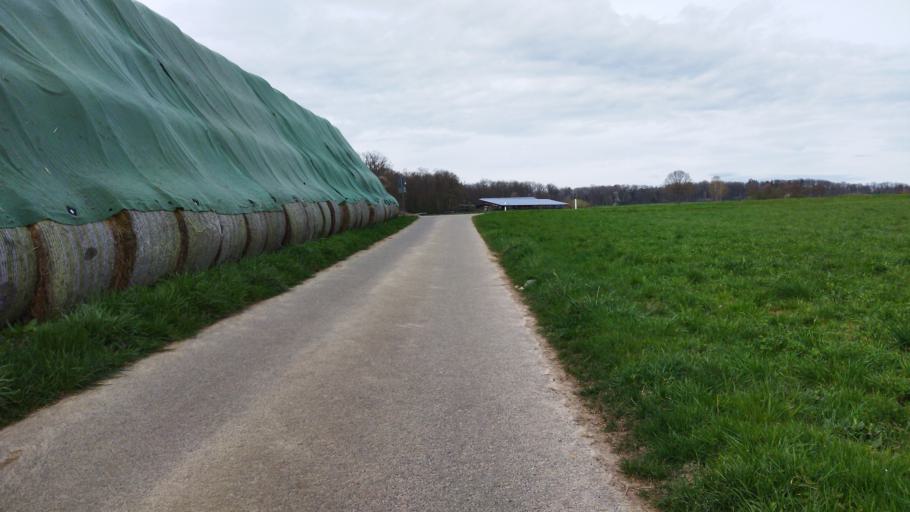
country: DE
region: Baden-Wuerttemberg
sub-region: Regierungsbezirk Stuttgart
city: Gundelsheim
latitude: 49.2937
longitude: 9.1889
